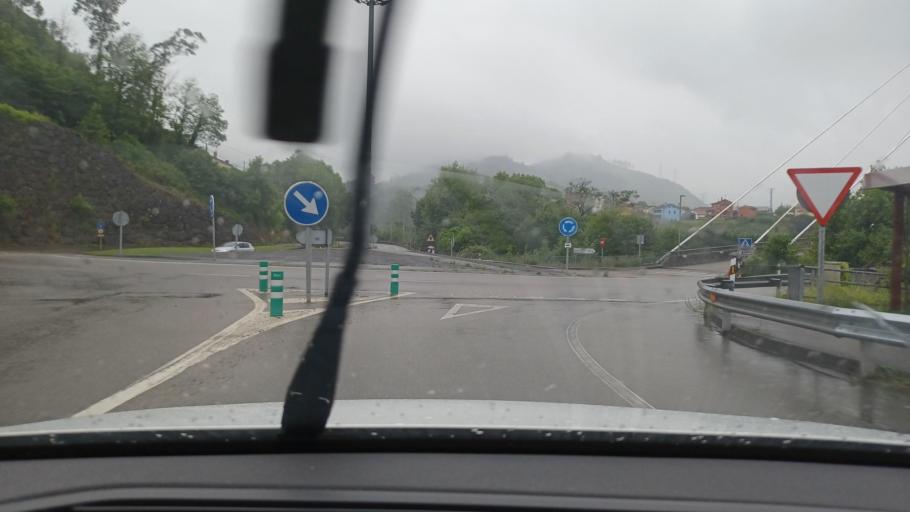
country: ES
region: Asturias
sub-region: Province of Asturias
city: Castandiello
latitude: 43.3098
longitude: -5.8714
